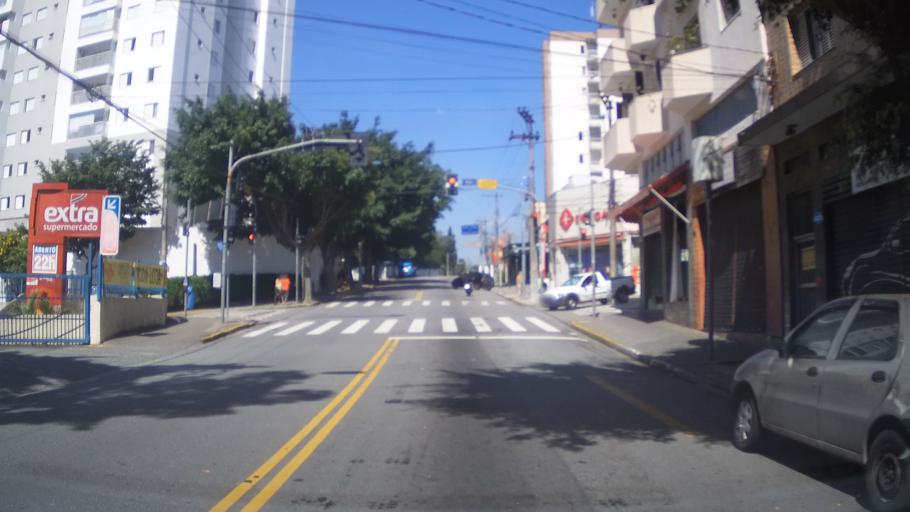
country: BR
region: Sao Paulo
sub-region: Sao Caetano Do Sul
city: Sao Caetano do Sul
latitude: -23.6434
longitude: -46.5612
